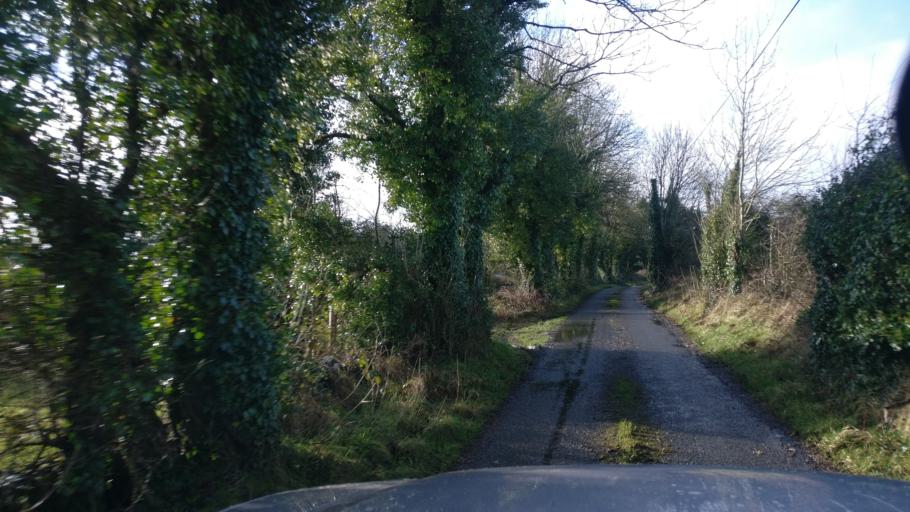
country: IE
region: Connaught
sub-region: County Galway
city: Loughrea
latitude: 53.2494
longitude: -8.6151
